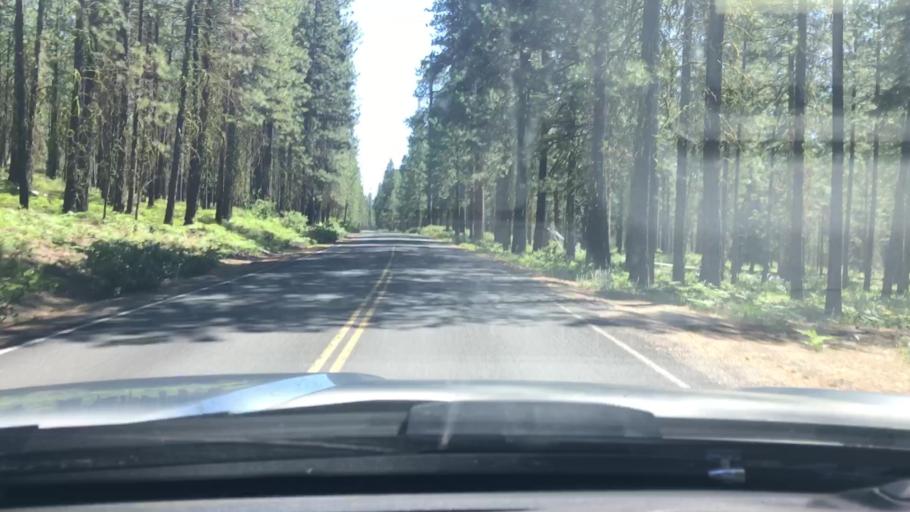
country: US
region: Oregon
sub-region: Deschutes County
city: Sisters
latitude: 44.4096
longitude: -121.6736
